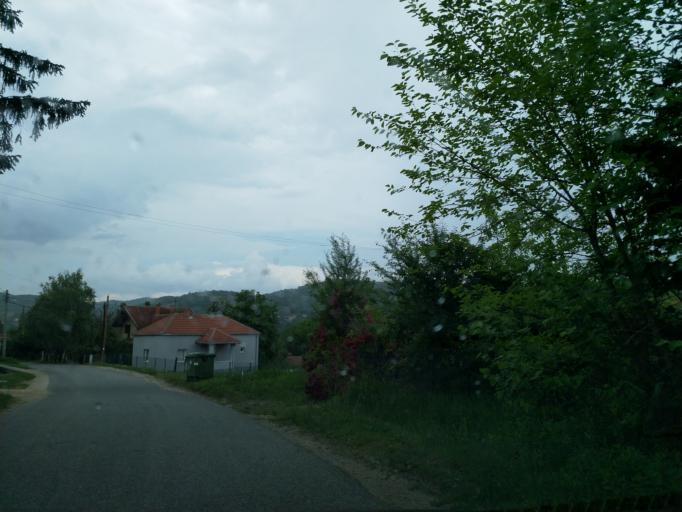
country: RS
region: Central Serbia
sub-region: Borski Okrug
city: Bor
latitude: 44.0064
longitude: 21.9841
